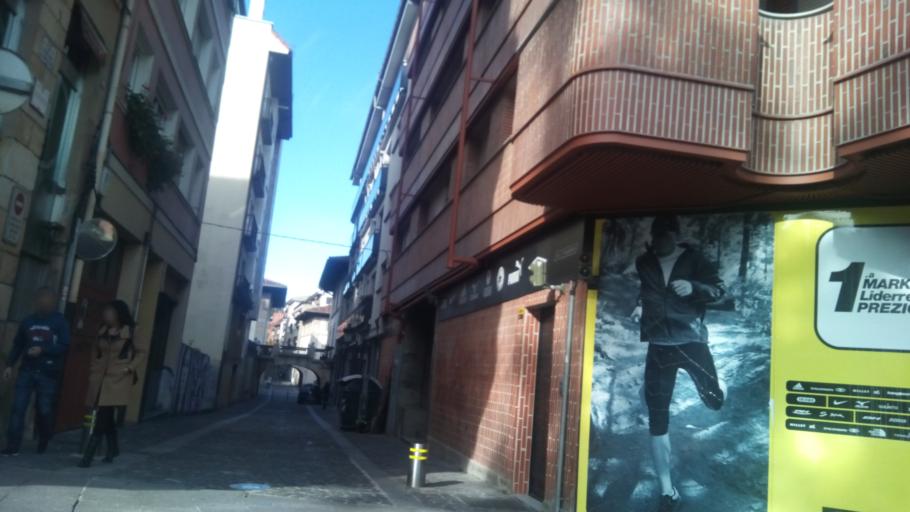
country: ES
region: Basque Country
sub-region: Bizkaia
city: Gernika-Lumo
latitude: 43.3144
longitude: -2.6784
